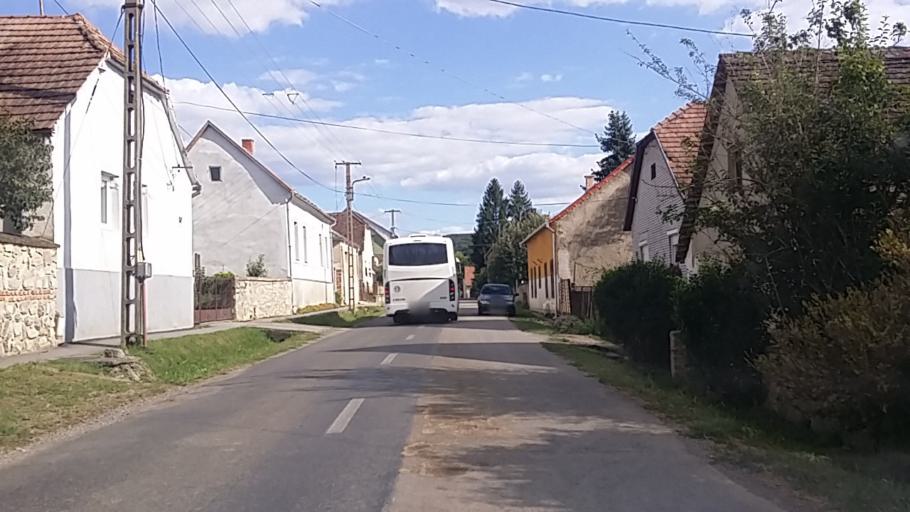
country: HU
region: Baranya
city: Sasd
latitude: 46.1449
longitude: 18.1138
